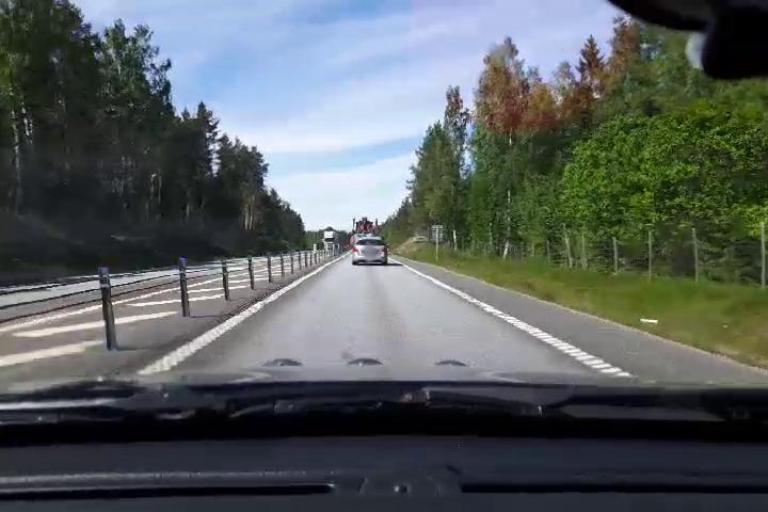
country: SE
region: Gaevleborg
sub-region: Gavle Kommun
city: Norrsundet
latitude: 61.0119
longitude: 16.9818
